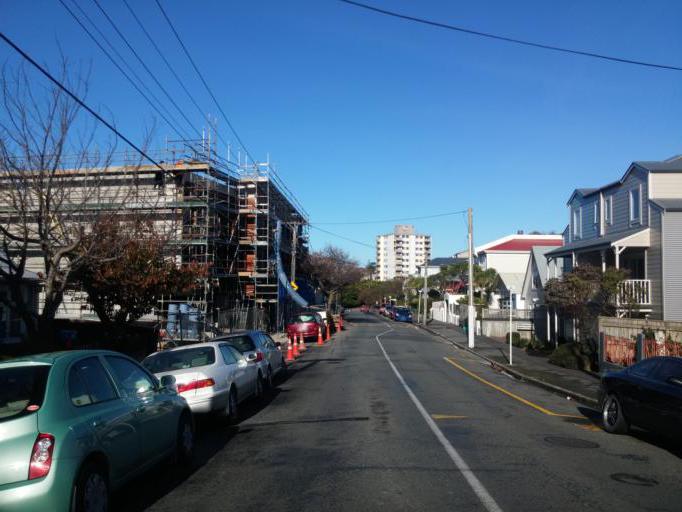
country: NZ
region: Wellington
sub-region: Wellington City
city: Wellington
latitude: -41.3053
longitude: 174.7763
